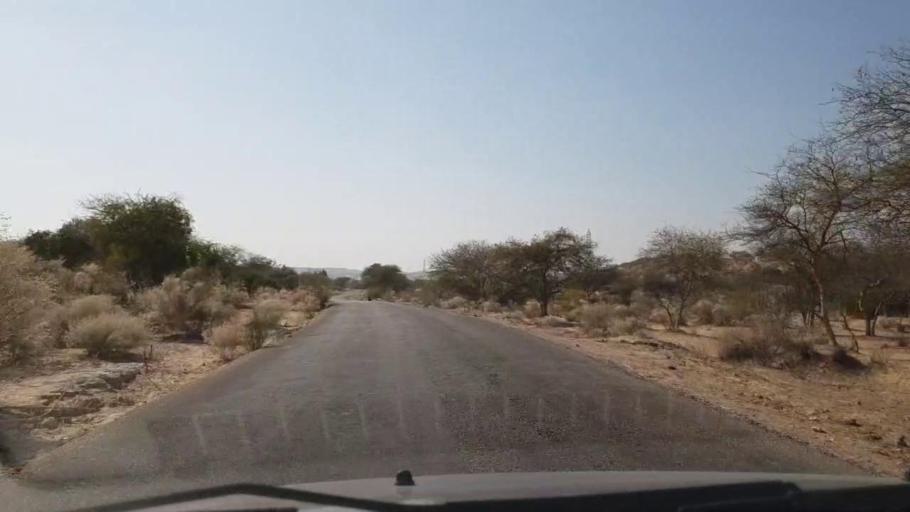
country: PK
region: Sindh
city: Mithi
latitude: 24.6726
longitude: 69.7692
